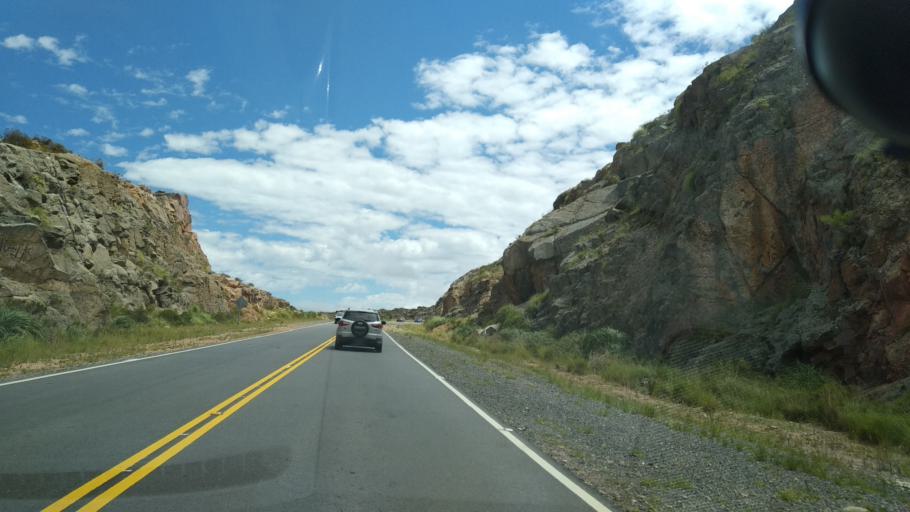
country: AR
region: Cordoba
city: Mina Clavero
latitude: -31.7463
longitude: -64.9092
